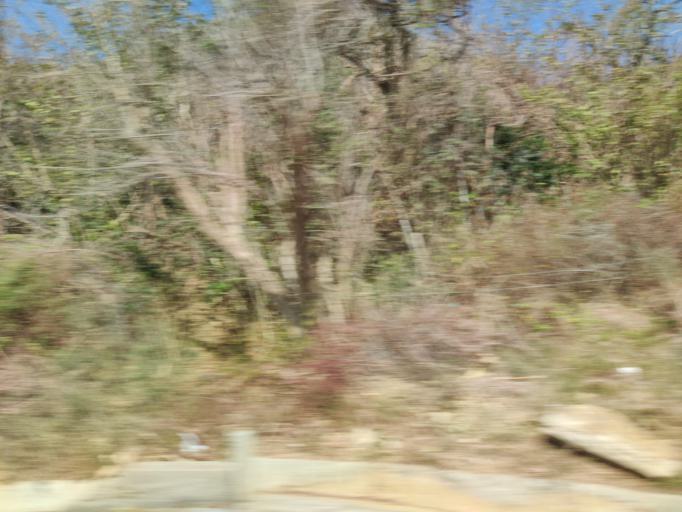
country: CO
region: Atlantico
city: Puerto Colombia
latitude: 10.9586
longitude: -75.0019
